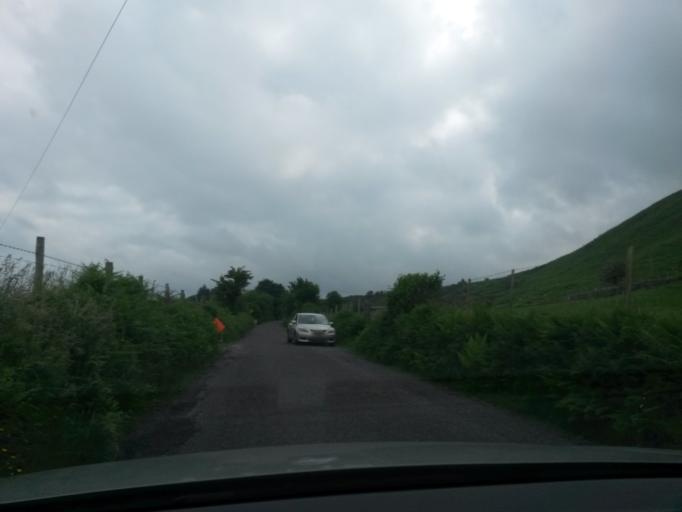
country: IE
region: Munster
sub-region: Ciarrai
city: Killorglin
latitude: 52.0382
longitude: -9.7870
